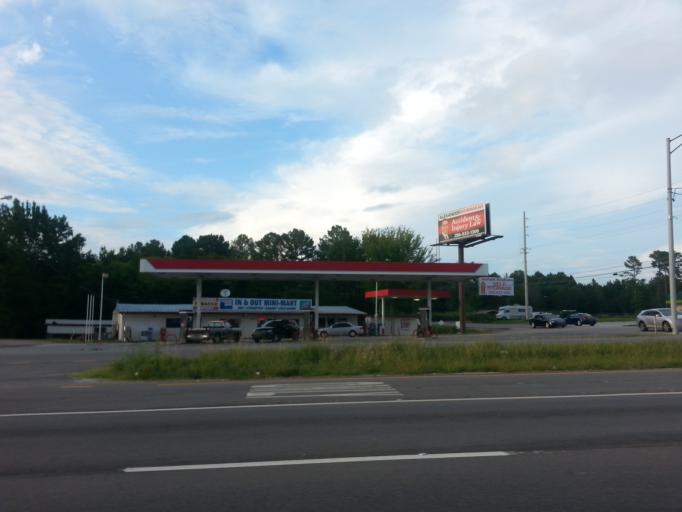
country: US
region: Alabama
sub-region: Madison County
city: Madison
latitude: 34.7477
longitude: -86.7865
